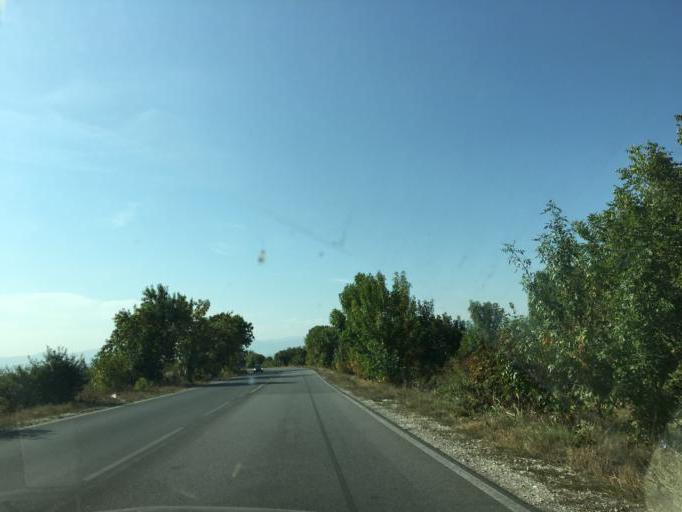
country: BG
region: Pazardzhik
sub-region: Obshtina Pazardzhik
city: Pazardzhik
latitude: 42.2259
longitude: 24.3103
